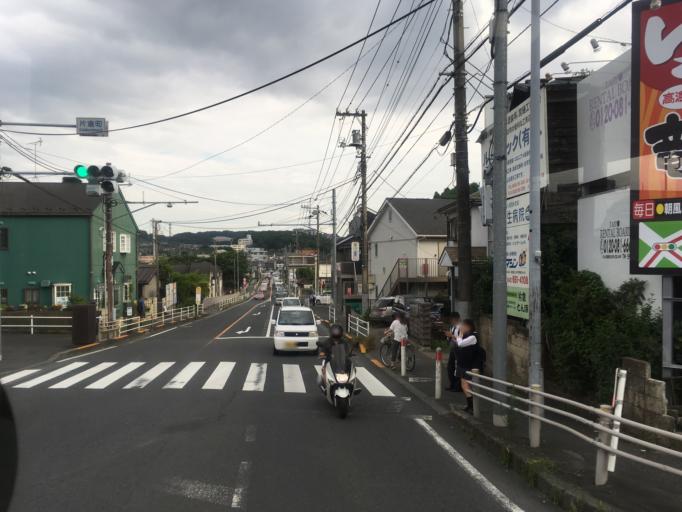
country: JP
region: Tokyo
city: Hachioji
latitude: 35.6428
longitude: 139.3388
